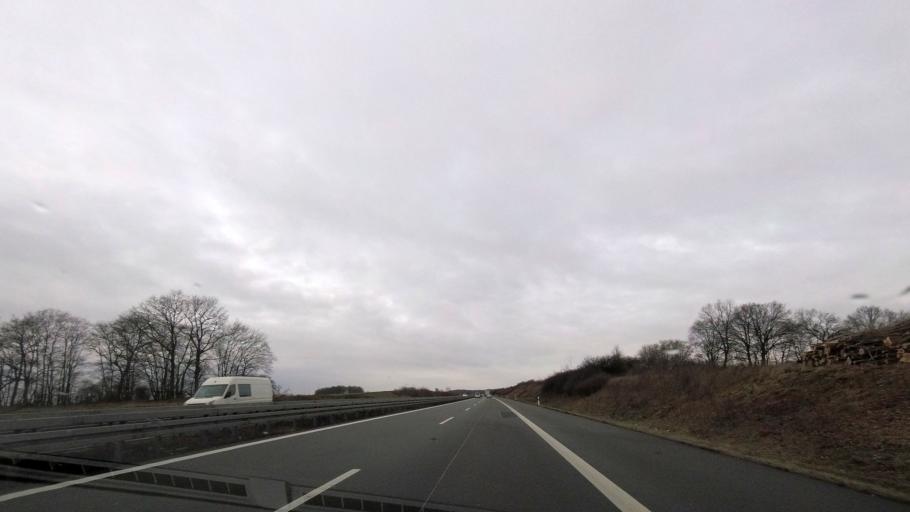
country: DE
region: Brandenburg
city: Gerdshagen
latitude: 53.2457
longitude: 12.1814
